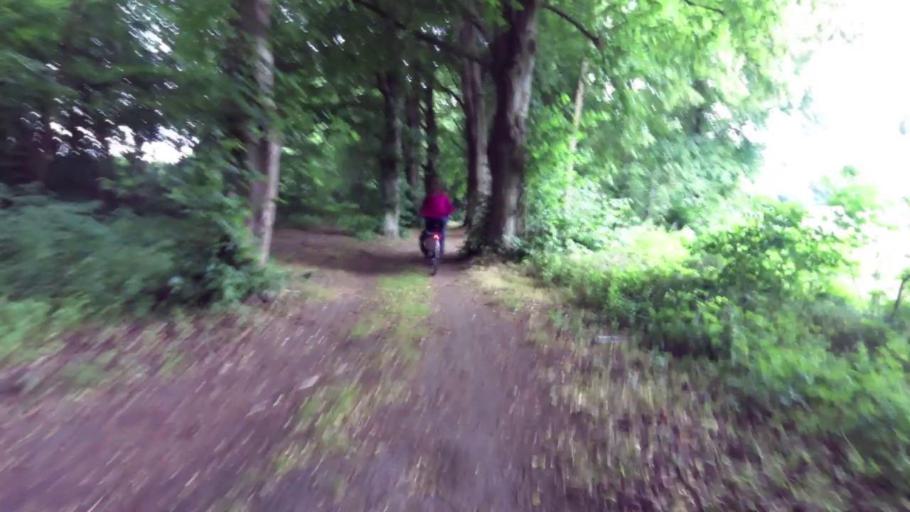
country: PL
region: West Pomeranian Voivodeship
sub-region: Powiat stargardzki
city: Chociwel
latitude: 53.4654
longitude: 15.3486
